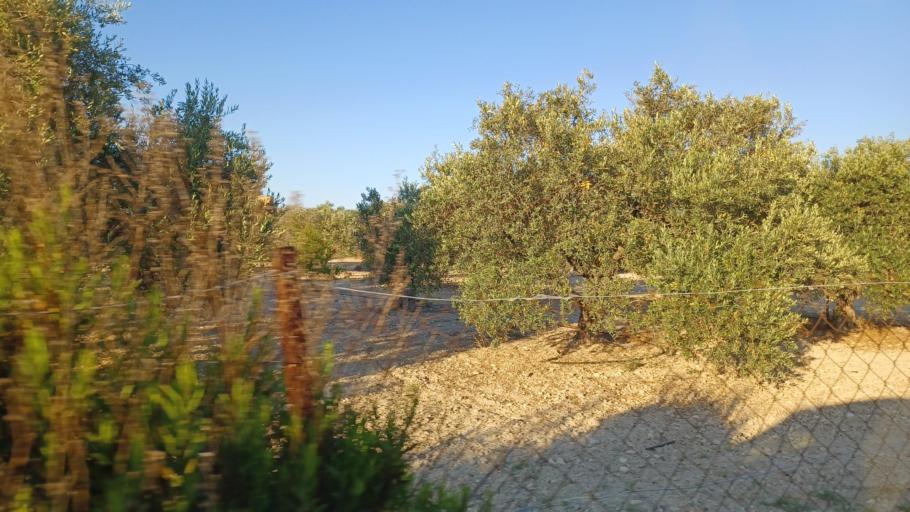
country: CY
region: Larnaka
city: Voroklini
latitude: 34.9839
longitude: 33.6724
